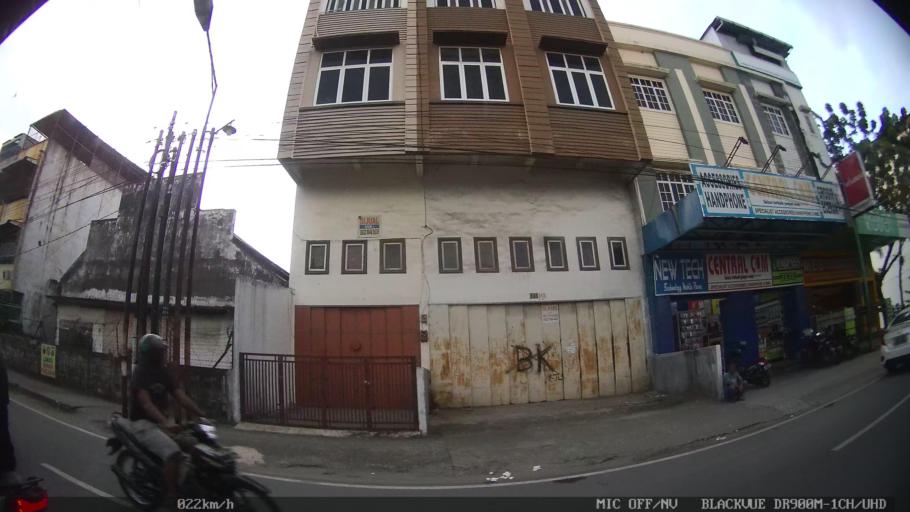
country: ID
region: North Sumatra
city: Medan
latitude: 3.5821
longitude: 98.6971
